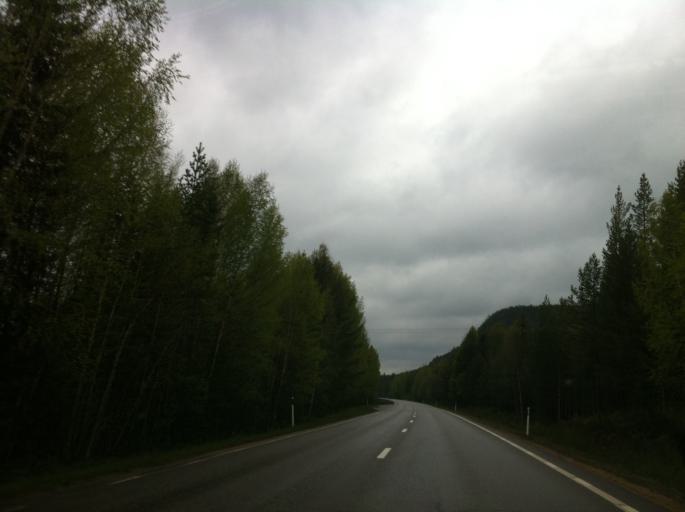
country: SE
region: Jaemtland
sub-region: Harjedalens Kommun
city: Sveg
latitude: 62.0961
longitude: 14.2334
